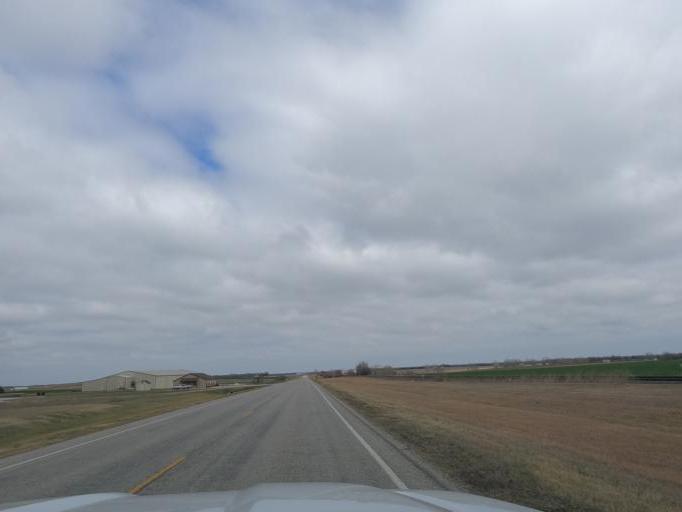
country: US
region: Kansas
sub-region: McPherson County
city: Inman
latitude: 38.2374
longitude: -97.7737
